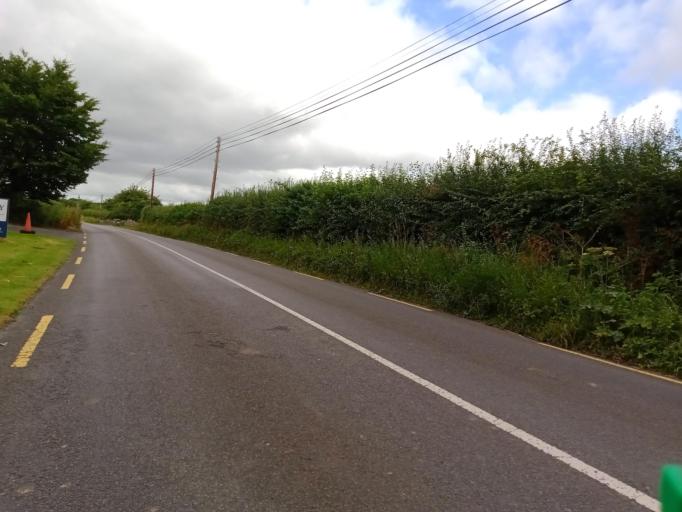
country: IE
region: Leinster
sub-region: Kilkenny
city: Callan
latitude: 52.5584
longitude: -7.4095
